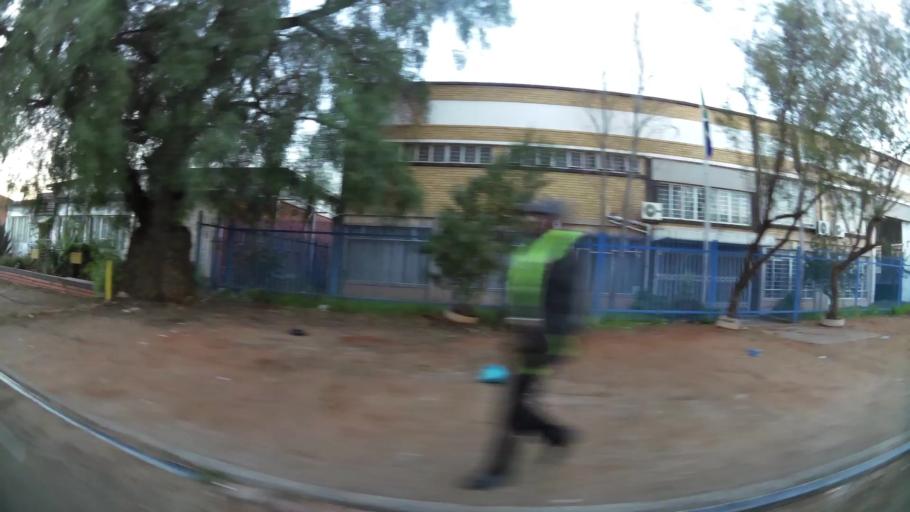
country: ZA
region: Northern Cape
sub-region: Frances Baard District Municipality
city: Kimberley
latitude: -28.7290
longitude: 24.7742
